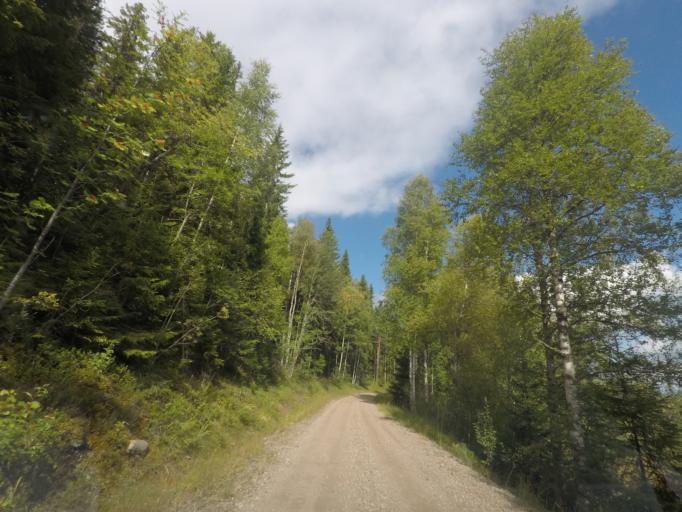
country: SE
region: Vaermland
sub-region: Filipstads Kommun
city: Lesjofors
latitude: 60.0457
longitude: 14.4440
